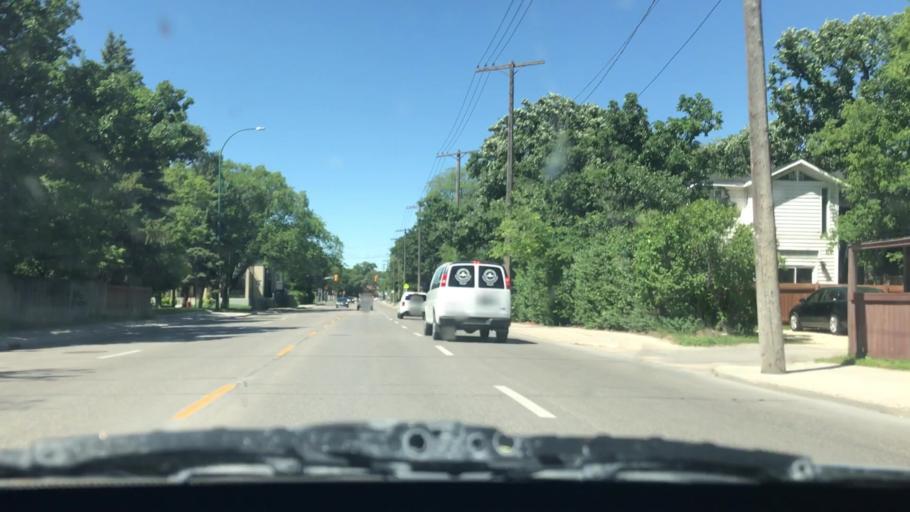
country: CA
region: Manitoba
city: Winnipeg
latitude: 49.8718
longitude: -97.1644
